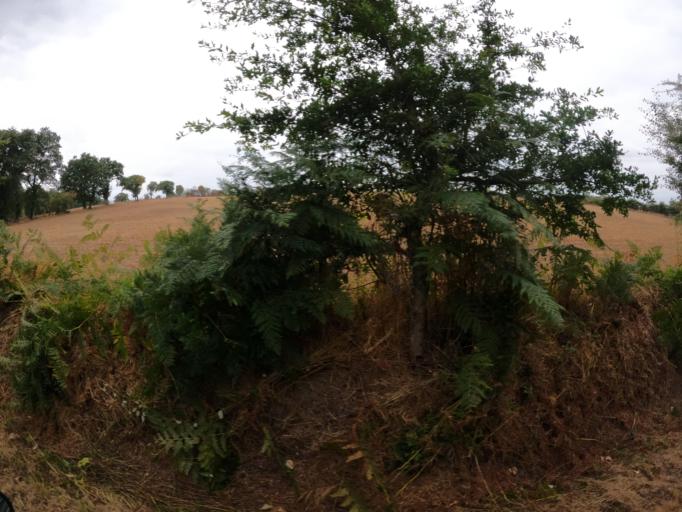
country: FR
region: Pays de la Loire
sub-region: Departement de Maine-et-Loire
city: Le Longeron
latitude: 46.9970
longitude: -1.0748
